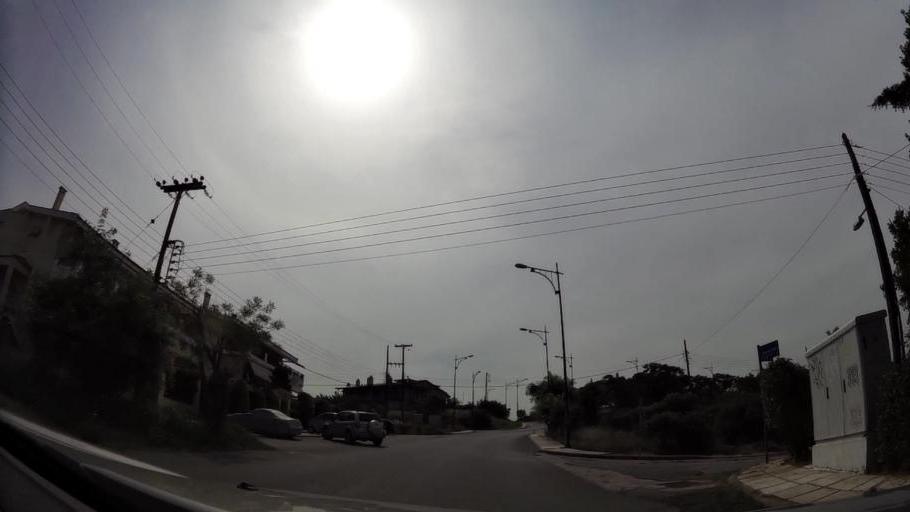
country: GR
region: Central Macedonia
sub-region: Nomos Thessalonikis
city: Panorama
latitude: 40.5802
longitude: 23.0104
